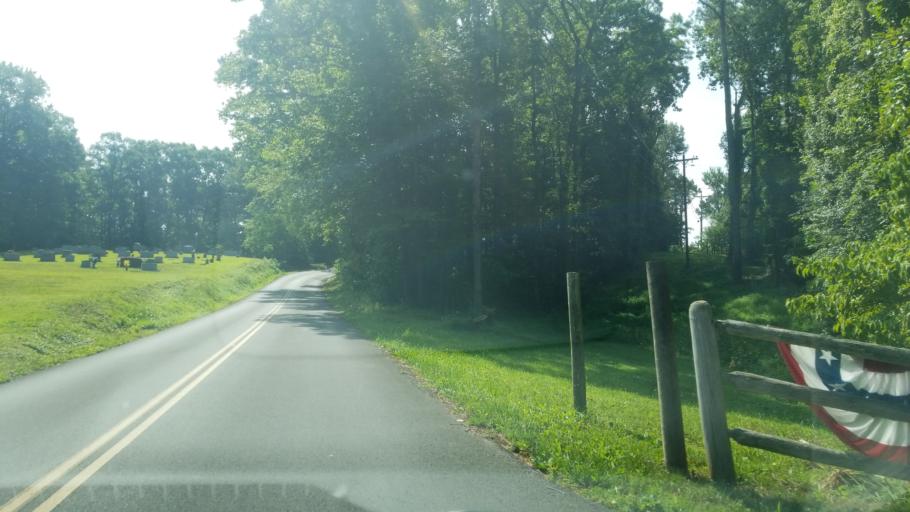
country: US
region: Tennessee
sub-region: Hamilton County
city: Apison
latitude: 35.0698
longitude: -84.9802
